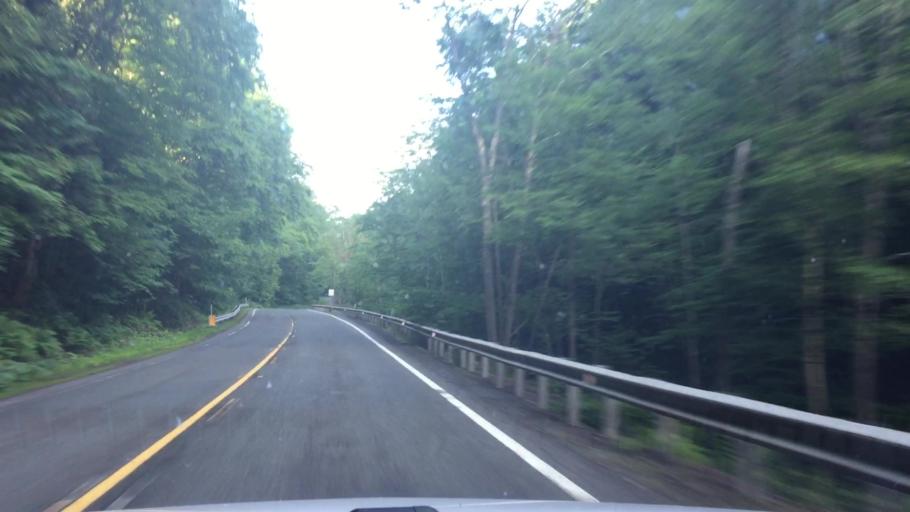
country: US
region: Massachusetts
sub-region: Hampshire County
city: Chesterfield
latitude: 42.3281
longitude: -72.8742
